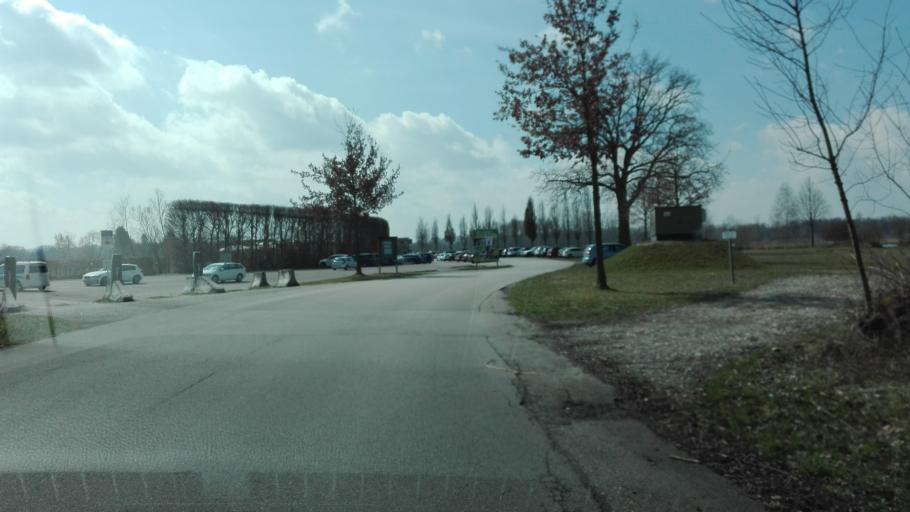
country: AT
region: Upper Austria
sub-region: Politischer Bezirk Urfahr-Umgebung
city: Feldkirchen an der Donau
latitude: 48.3282
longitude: 14.0713
